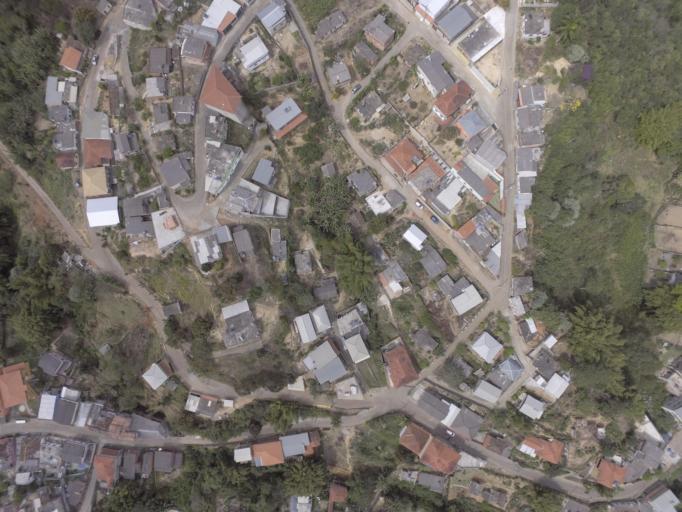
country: BR
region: Minas Gerais
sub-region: Tiradentes
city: Tiradentes
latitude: -21.0550
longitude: -44.0747
